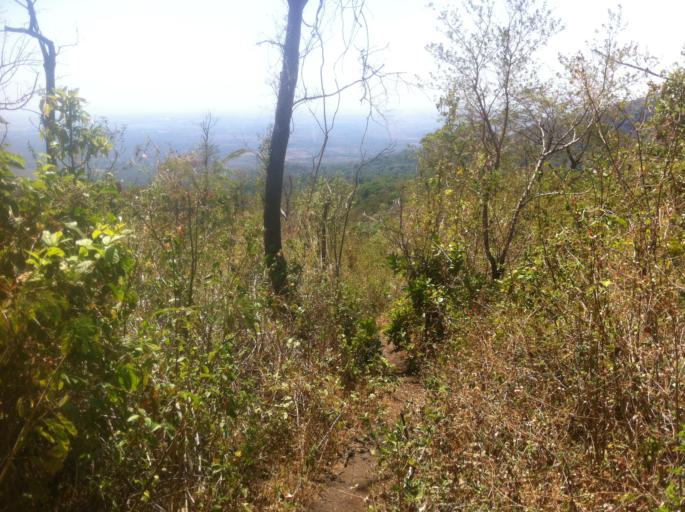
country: NI
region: Chinandega
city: Chichigalpa
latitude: 12.6961
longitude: -87.0234
